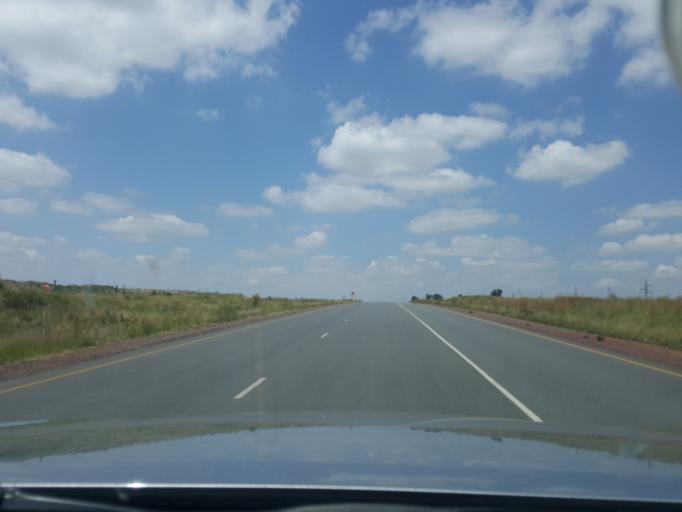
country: ZA
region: Mpumalanga
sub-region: Nkangala District Municipality
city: Witbank
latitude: -26.0142
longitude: 29.3776
